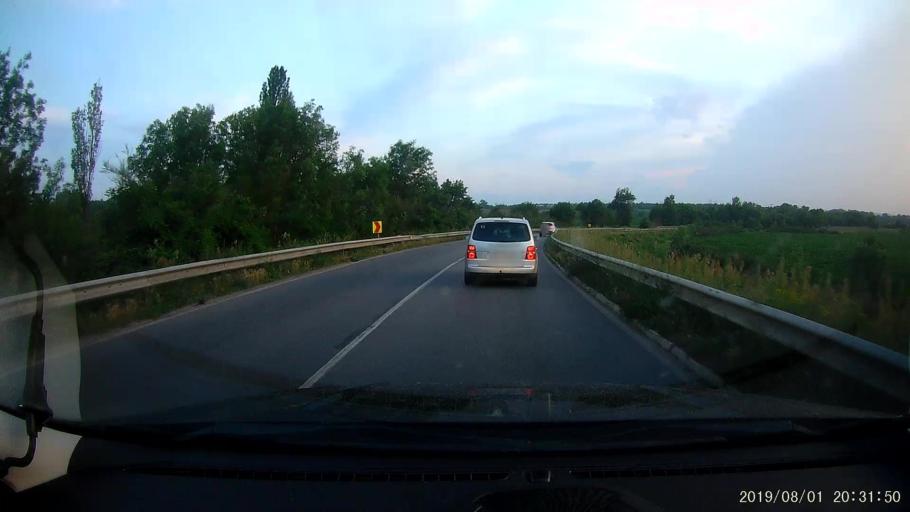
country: BG
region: Yambol
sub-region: Obshtina Elkhovo
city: Elkhovo
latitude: 42.1257
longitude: 26.5375
